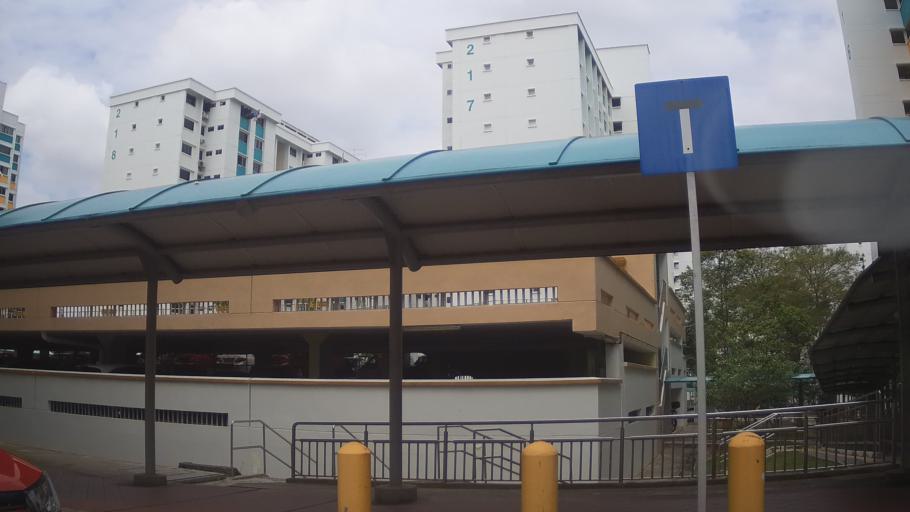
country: MY
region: Johor
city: Johor Bahru
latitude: 1.3742
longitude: 103.7747
